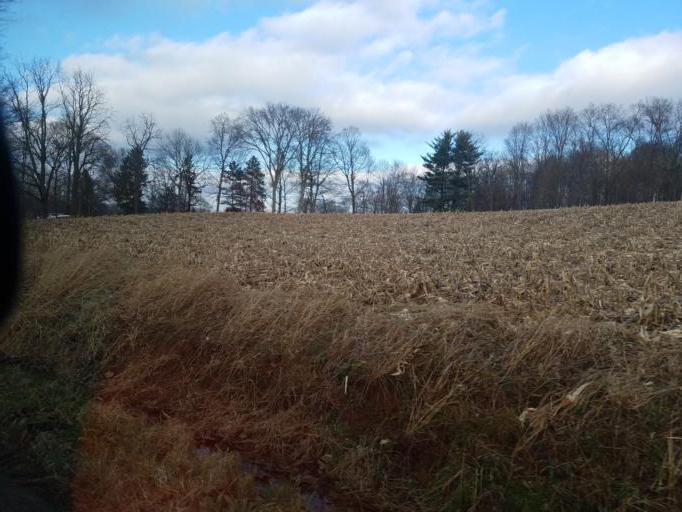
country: US
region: Ohio
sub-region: Ashland County
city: Loudonville
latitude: 40.6305
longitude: -82.3672
